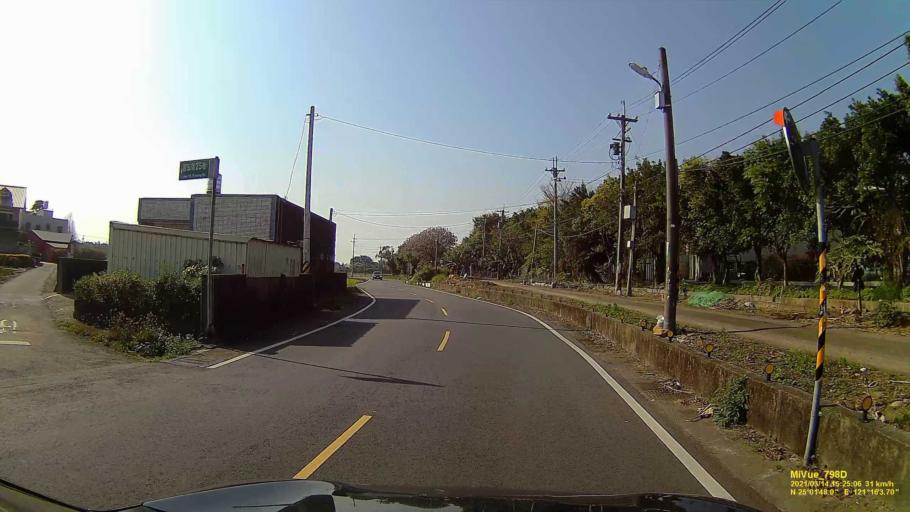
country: TW
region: Taiwan
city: Taoyuan City
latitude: 25.0301
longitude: 121.2673
